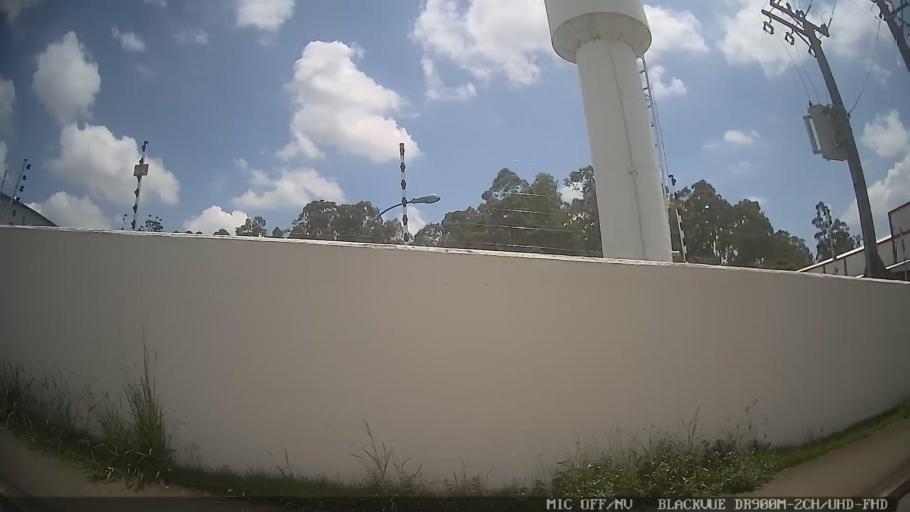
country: BR
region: Sao Paulo
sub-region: Jacarei
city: Jacarei
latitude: -23.3027
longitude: -46.0164
